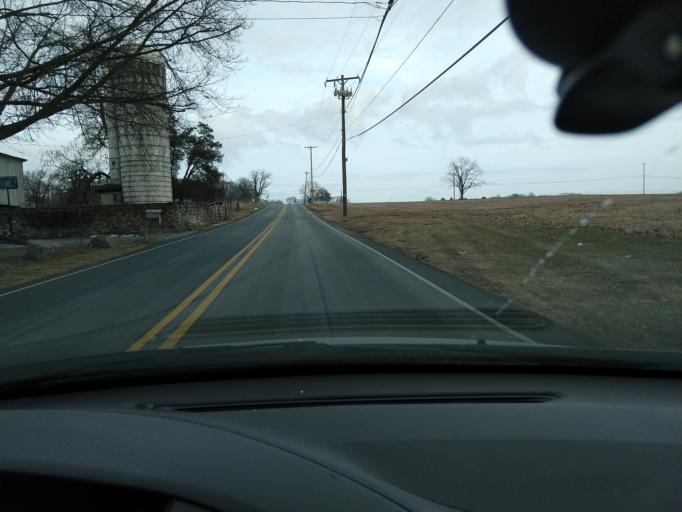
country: US
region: Pennsylvania
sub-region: Chester County
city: South Pottstown
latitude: 40.2030
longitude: -75.6714
